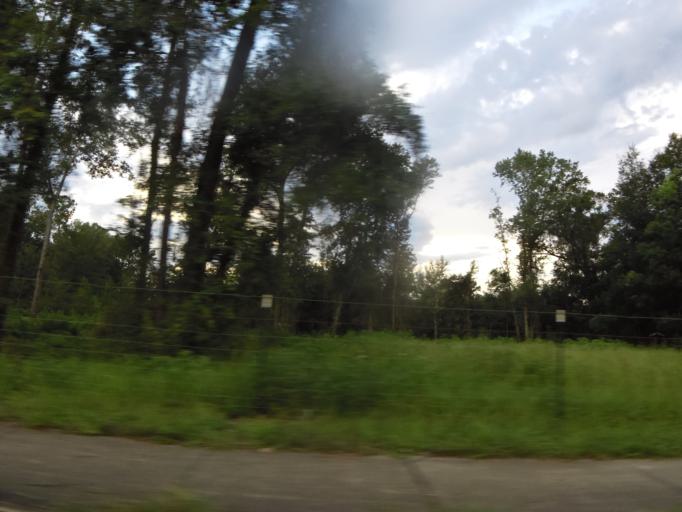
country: US
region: Florida
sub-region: Clay County
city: Bellair-Meadowbrook Terrace
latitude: 30.2947
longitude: -81.7814
